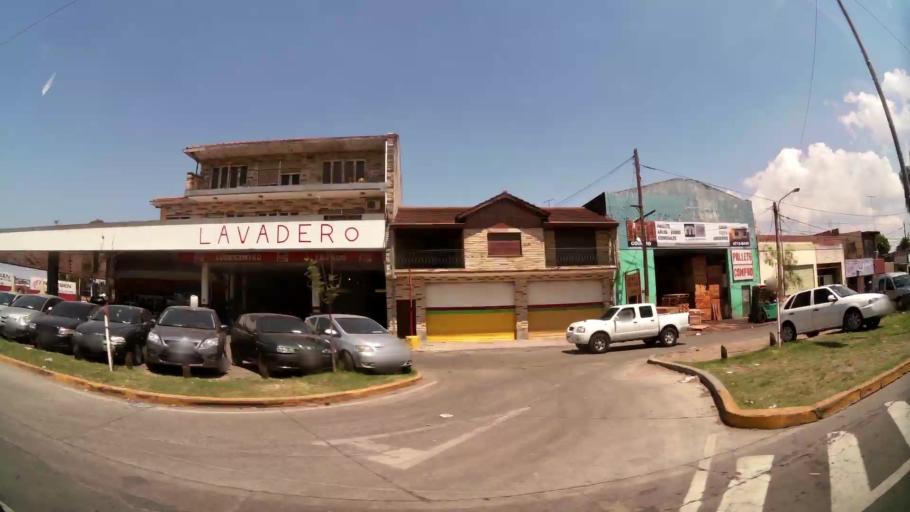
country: AR
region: Buenos Aires
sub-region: Partido de Tigre
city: Tigre
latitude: -34.4448
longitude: -58.5982
